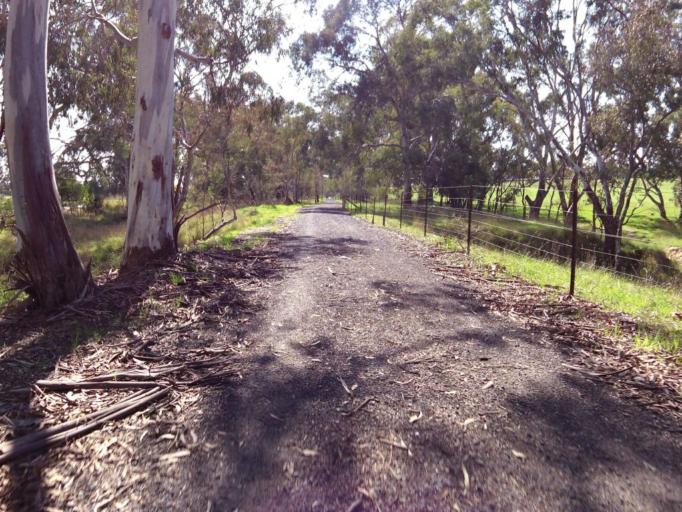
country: AU
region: Victoria
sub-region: Murrindindi
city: Alexandra
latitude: -37.1195
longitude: 145.6034
